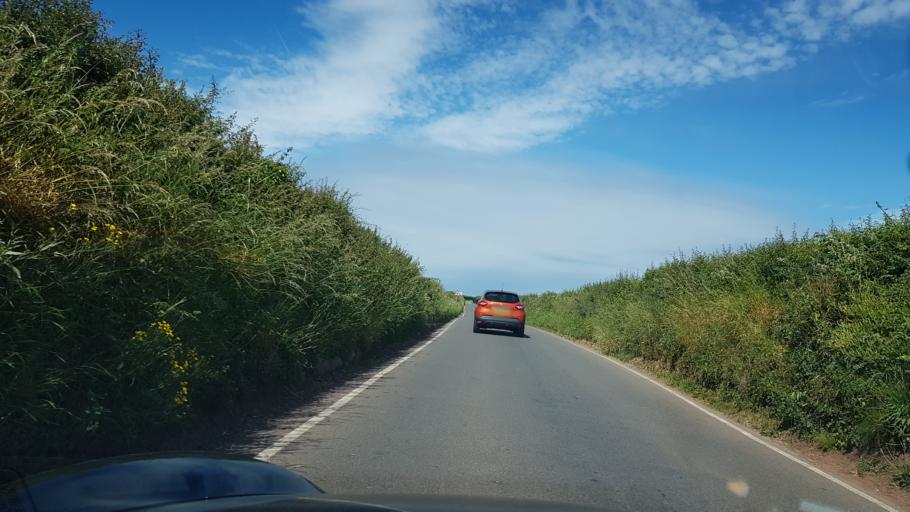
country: GB
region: Wales
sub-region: Pembrokeshire
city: Dale
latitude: 51.7499
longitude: -5.1367
